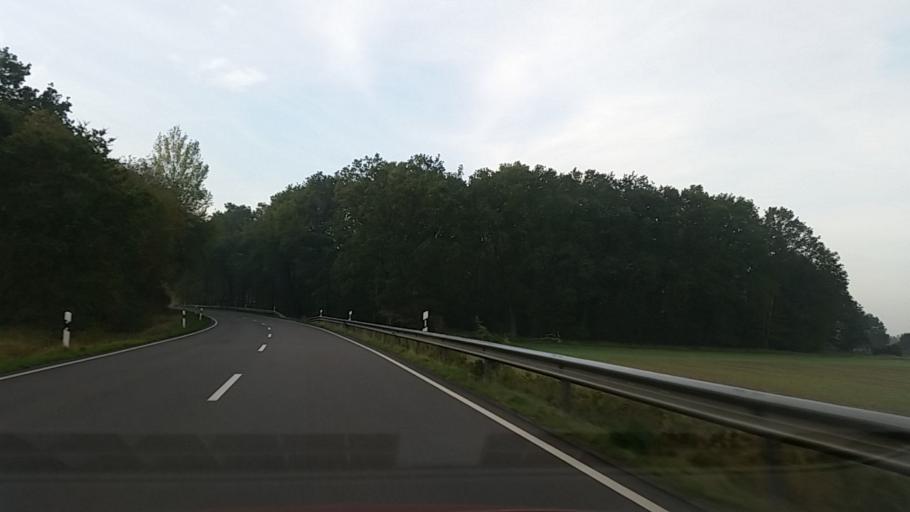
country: DE
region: Lower Saxony
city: Ruhen
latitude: 52.5005
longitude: 10.8812
